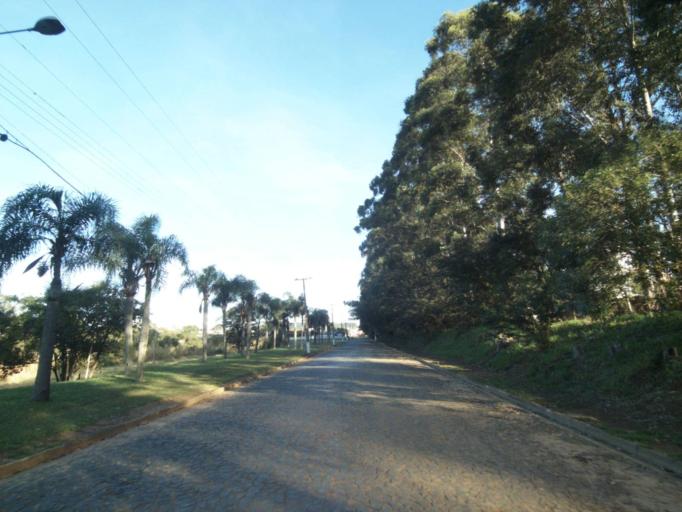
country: BR
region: Parana
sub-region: Tibagi
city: Tibagi
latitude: -24.5056
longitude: -50.4173
